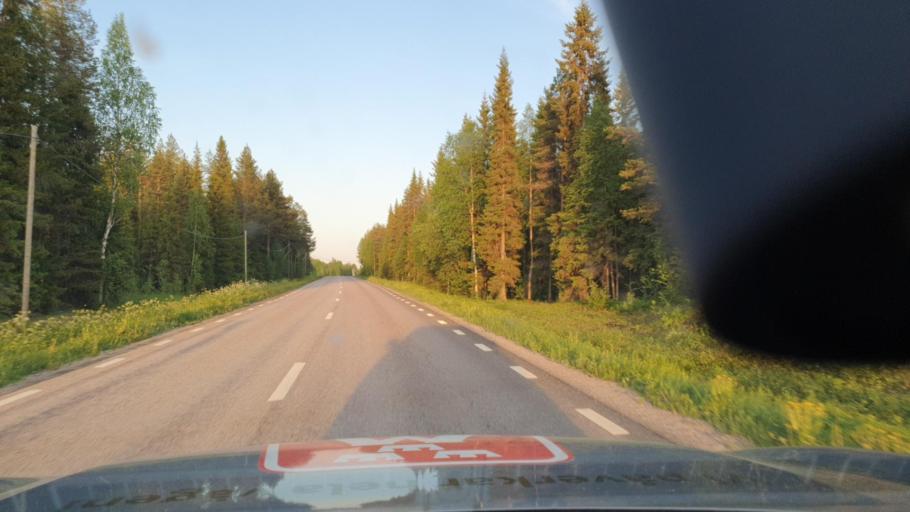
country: SE
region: Norrbotten
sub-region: Bodens Kommun
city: Saevast
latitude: 65.8854
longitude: 21.8508
